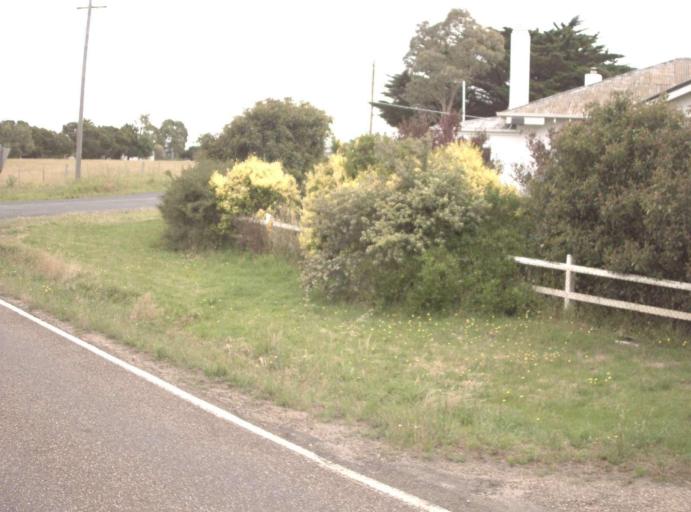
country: AU
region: Victoria
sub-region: East Gippsland
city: Bairnsdale
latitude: -37.8206
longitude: 147.5018
